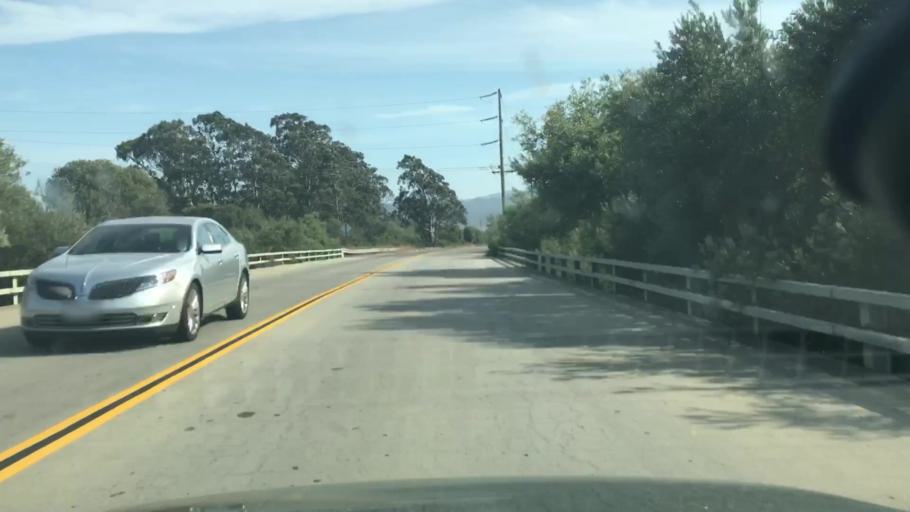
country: US
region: California
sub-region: Santa Barbara County
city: Vandenberg Village
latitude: 34.6722
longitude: -120.4932
